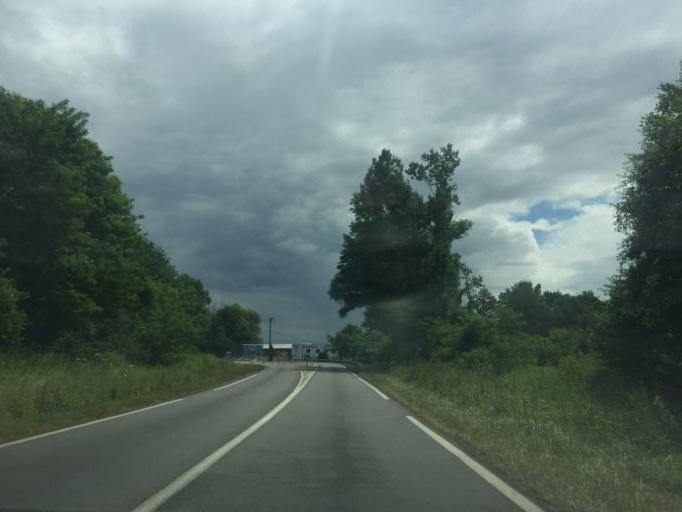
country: FR
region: Rhone-Alpes
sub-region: Departement de l'Isere
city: Charvieu-Chavagneux
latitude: 45.7537
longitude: 5.1370
